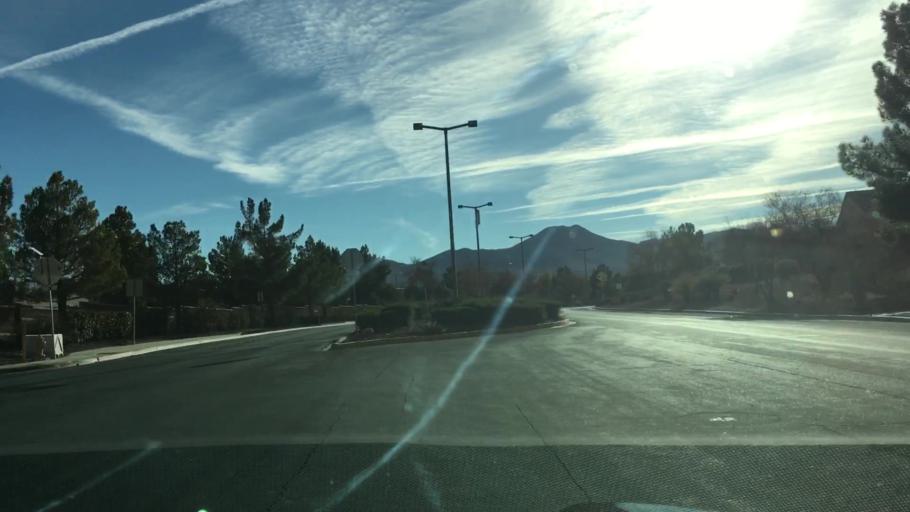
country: US
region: Nevada
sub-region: Clark County
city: Whitney
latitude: 35.9689
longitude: -115.1014
